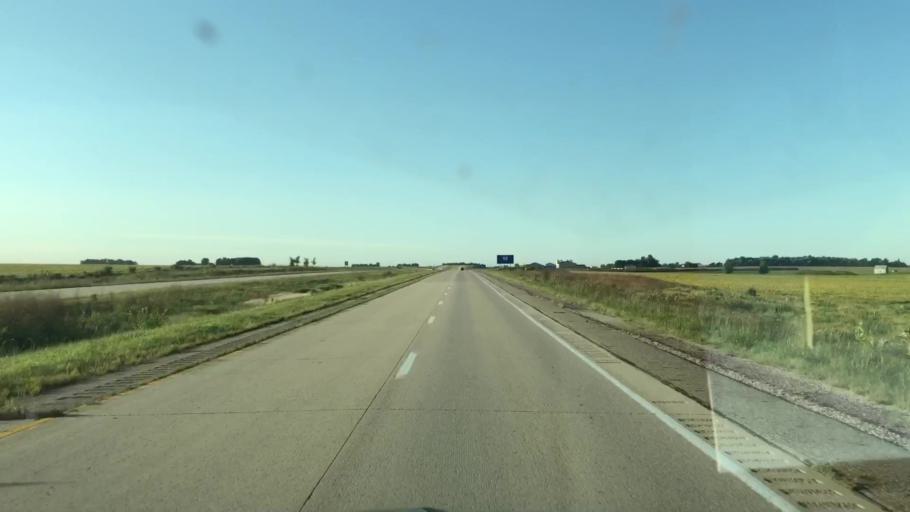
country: US
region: Iowa
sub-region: Osceola County
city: Sibley
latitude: 43.4470
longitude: -95.7136
